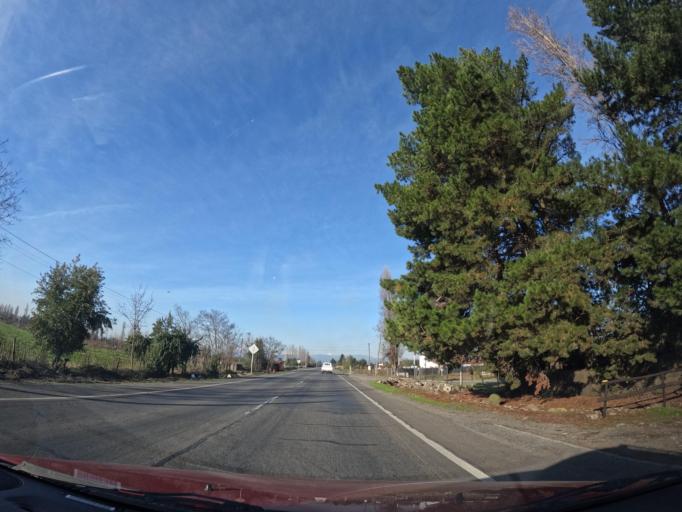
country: CL
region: Maule
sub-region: Provincia de Talca
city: San Clemente
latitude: -35.6273
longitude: -71.4729
